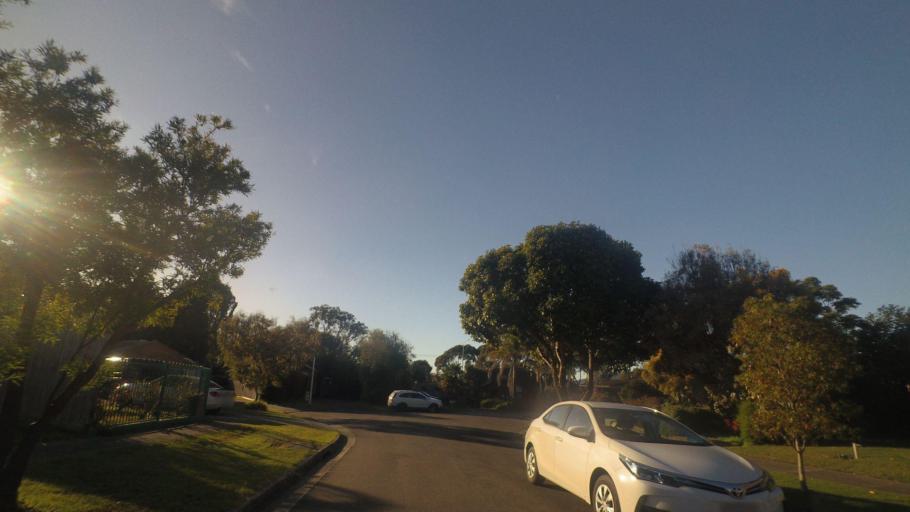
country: AU
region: Victoria
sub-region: Knox
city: Knoxfield
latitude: -37.9144
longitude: 145.2601
